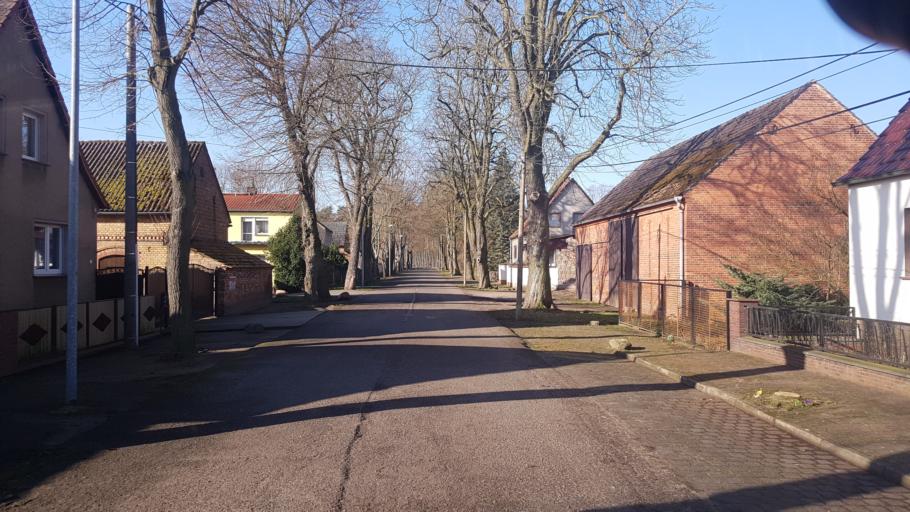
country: DE
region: Brandenburg
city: Lubbenau
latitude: 51.8385
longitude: 13.9262
